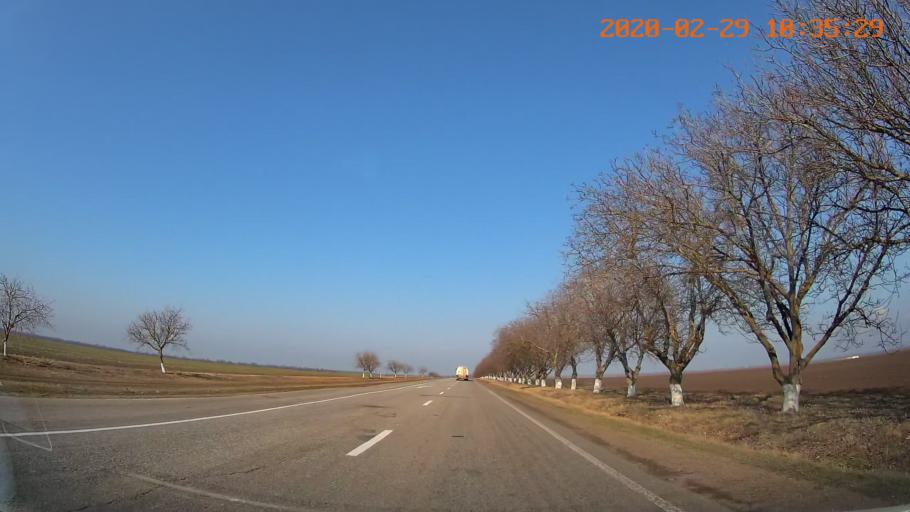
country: MD
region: Anenii Noi
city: Varnita
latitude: 46.9862
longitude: 29.5198
